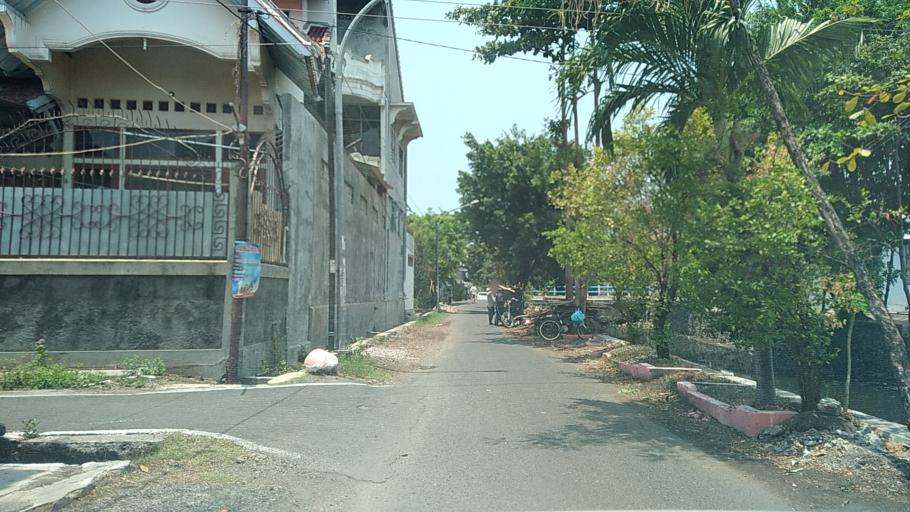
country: ID
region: Central Java
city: Semarang
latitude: -6.9805
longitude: 110.4373
